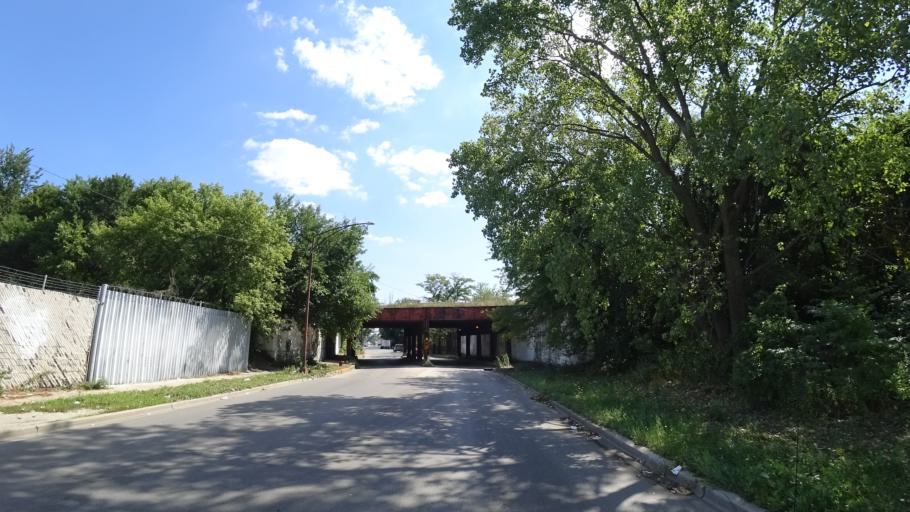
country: US
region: Illinois
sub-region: Cook County
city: Cicero
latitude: 41.8689
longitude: -87.7404
